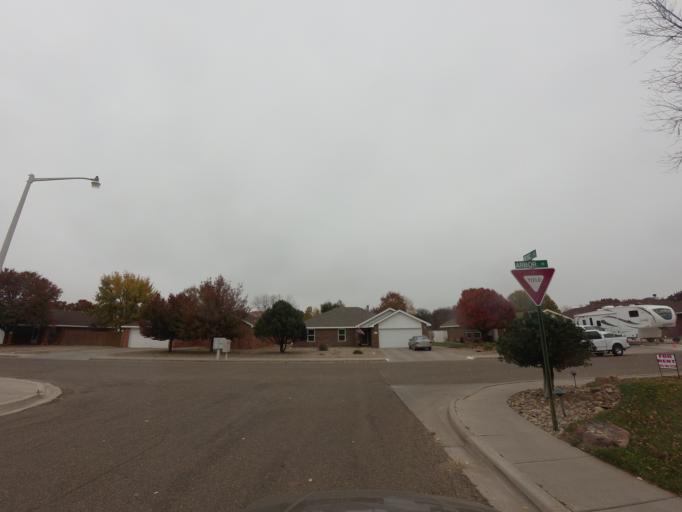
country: US
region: New Mexico
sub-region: Curry County
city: Clovis
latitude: 34.4279
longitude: -103.1840
